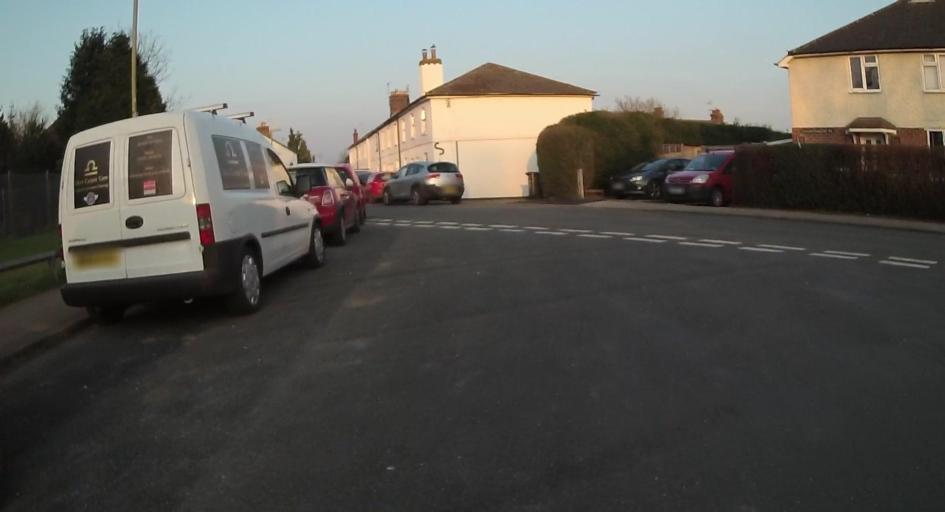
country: GB
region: England
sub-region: Hampshire
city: Alton
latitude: 51.1531
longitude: -0.9733
